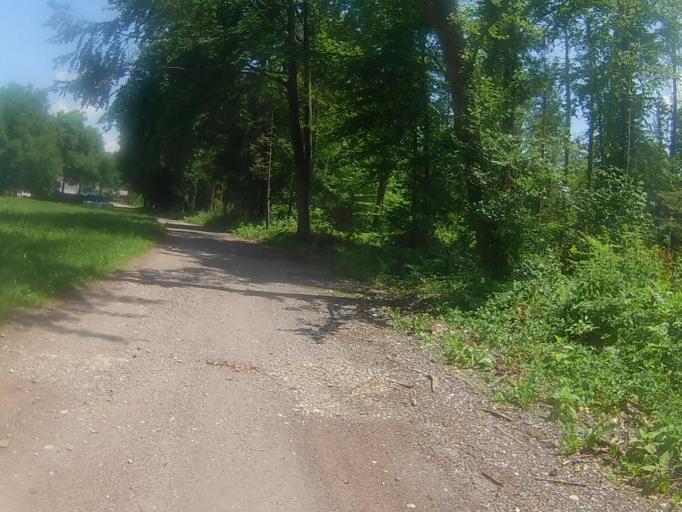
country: SI
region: Ruse
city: Bistrica ob Dravi
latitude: 46.5555
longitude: 15.5384
